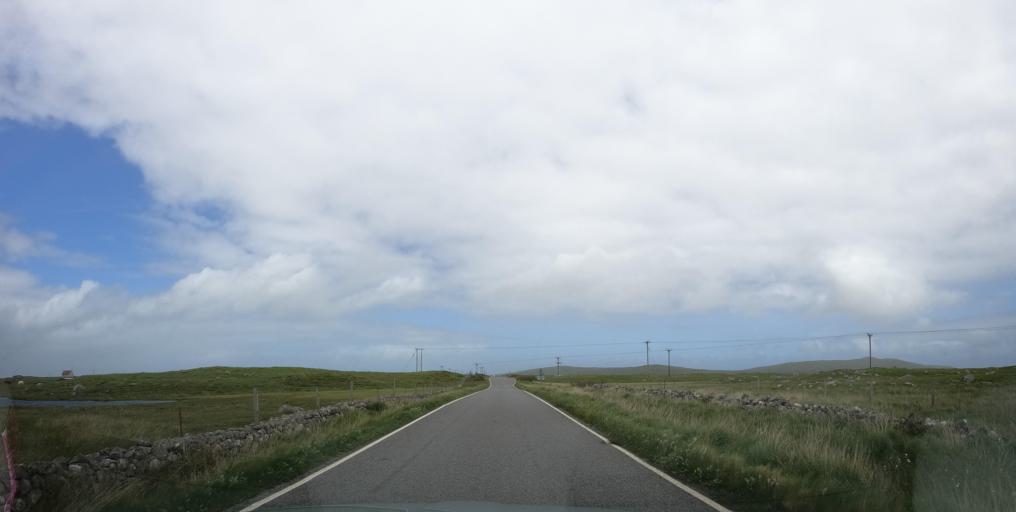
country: GB
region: Scotland
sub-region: Eilean Siar
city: Isle of South Uist
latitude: 57.3081
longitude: -7.3709
